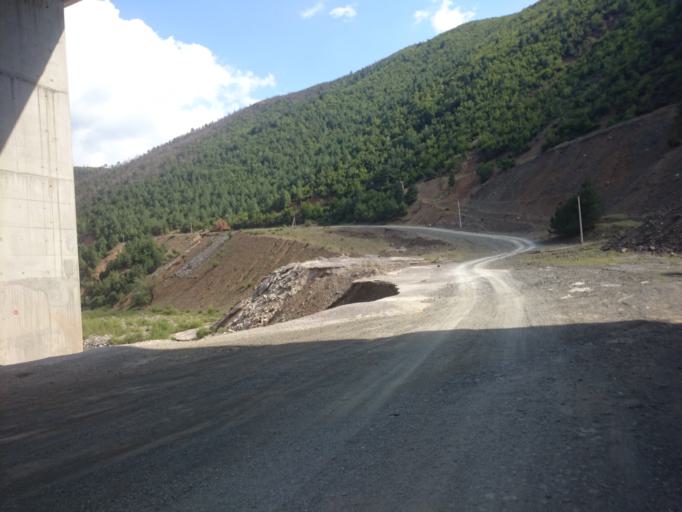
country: AL
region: Lezhe
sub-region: Rrethi i Lezhes
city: Blinisht
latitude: 41.8697
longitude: 20.0333
